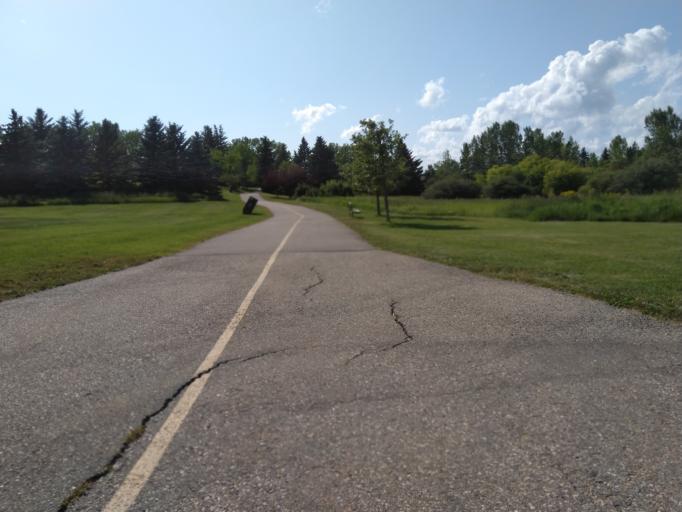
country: CA
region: Alberta
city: Calgary
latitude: 51.0790
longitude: -114.1069
